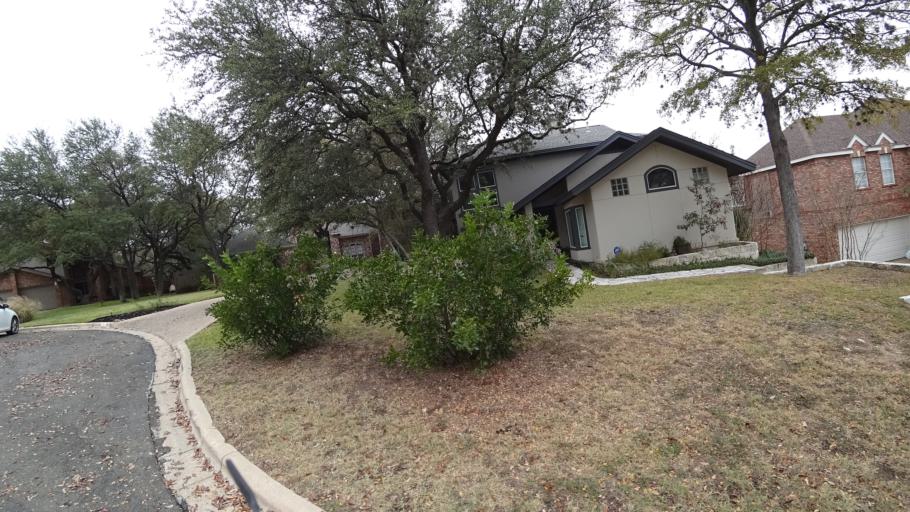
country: US
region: Texas
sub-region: Williamson County
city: Jollyville
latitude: 30.3779
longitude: -97.7980
